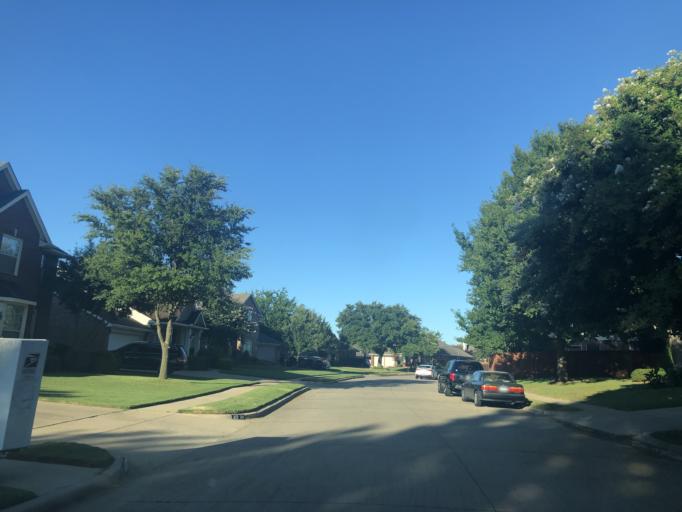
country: US
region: Texas
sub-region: Dallas County
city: Cedar Hill
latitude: 32.6615
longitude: -96.9976
